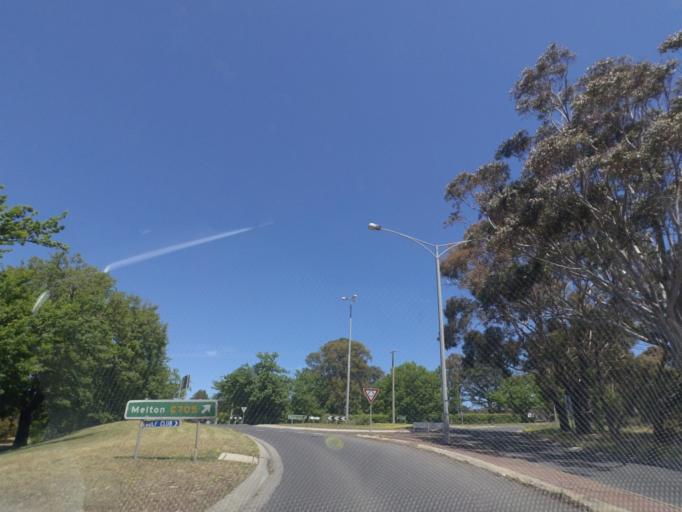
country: AU
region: Victoria
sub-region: Hume
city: Sunbury
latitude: -37.4935
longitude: 144.5899
